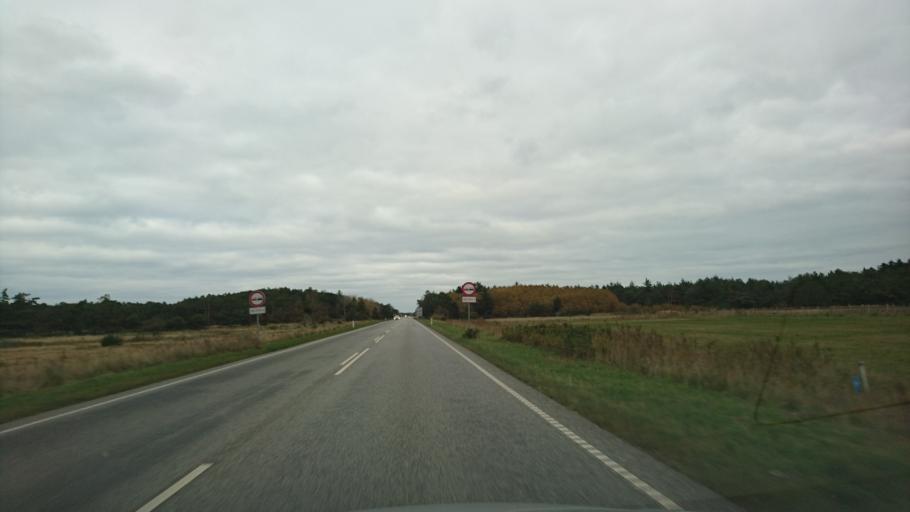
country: DK
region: North Denmark
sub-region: Frederikshavn Kommune
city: Skagen
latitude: 57.7167
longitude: 10.5320
